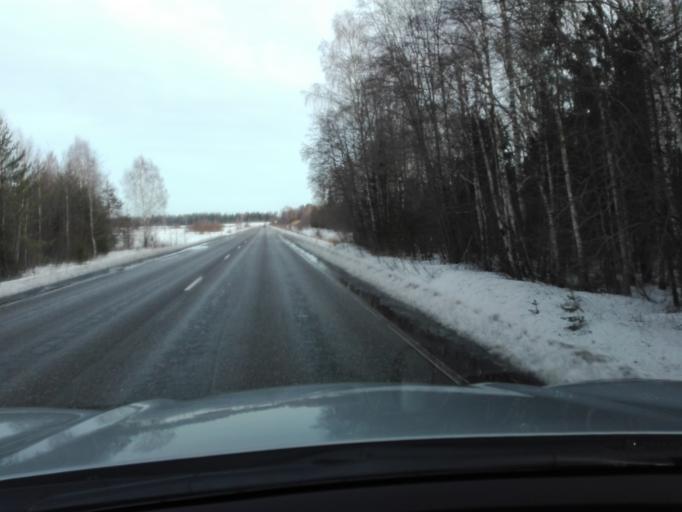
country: EE
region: Raplamaa
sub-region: Rapla vald
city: Rapla
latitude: 58.9734
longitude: 24.7721
